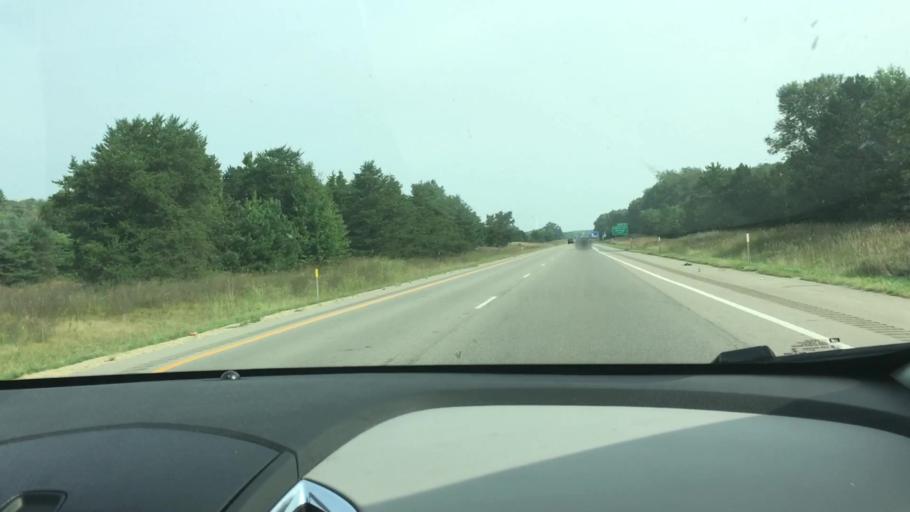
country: US
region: Michigan
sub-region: Kalamazoo County
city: Schoolcraft
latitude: 42.1769
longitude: -85.6452
